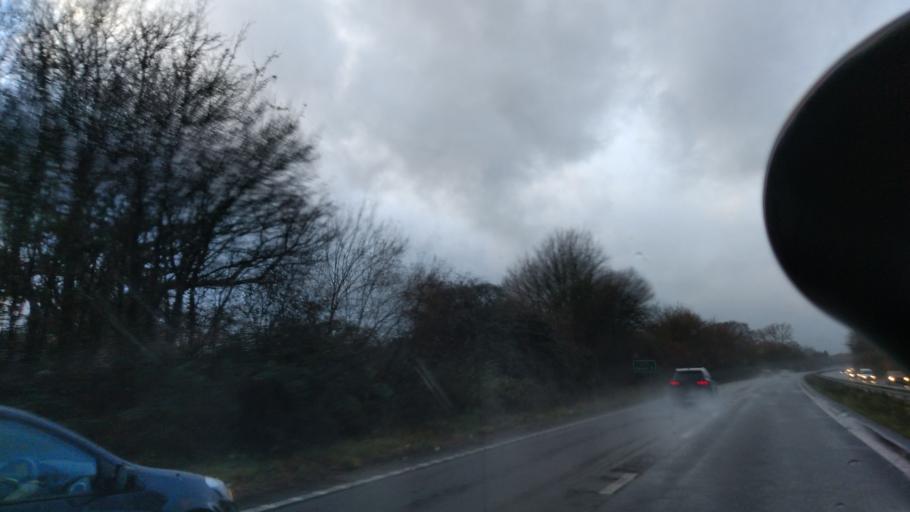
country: GB
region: England
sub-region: West Sussex
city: Bosham
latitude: 50.8527
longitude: -0.8687
